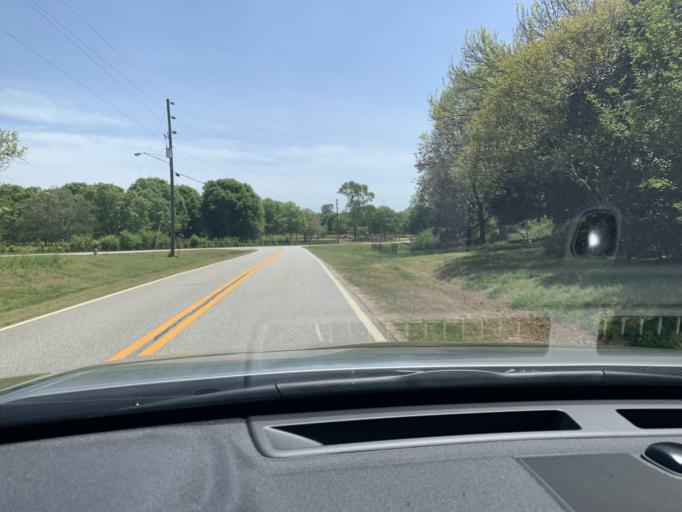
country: US
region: Georgia
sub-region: Oconee County
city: Bogart
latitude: 33.8494
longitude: -83.5338
